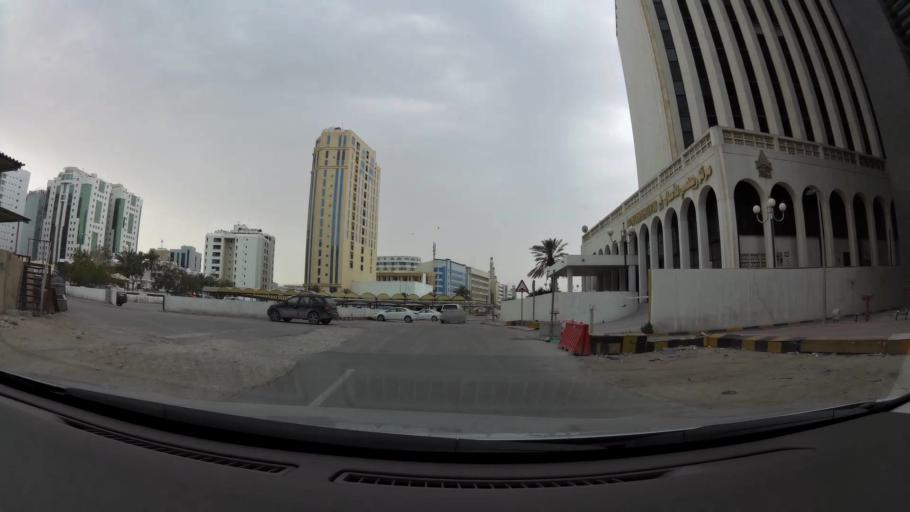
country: QA
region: Baladiyat ad Dawhah
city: Doha
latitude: 25.2901
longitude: 51.5416
